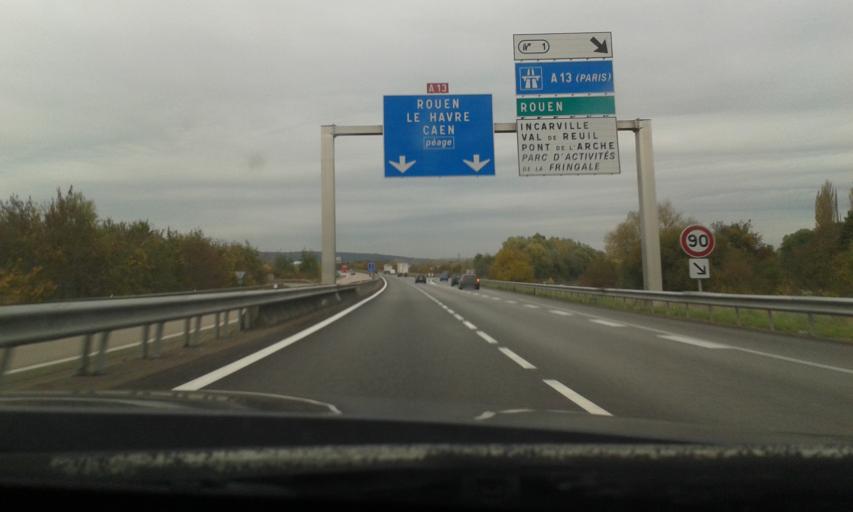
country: FR
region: Haute-Normandie
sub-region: Departement de l'Eure
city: Louviers
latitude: 49.2345
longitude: 1.1850
